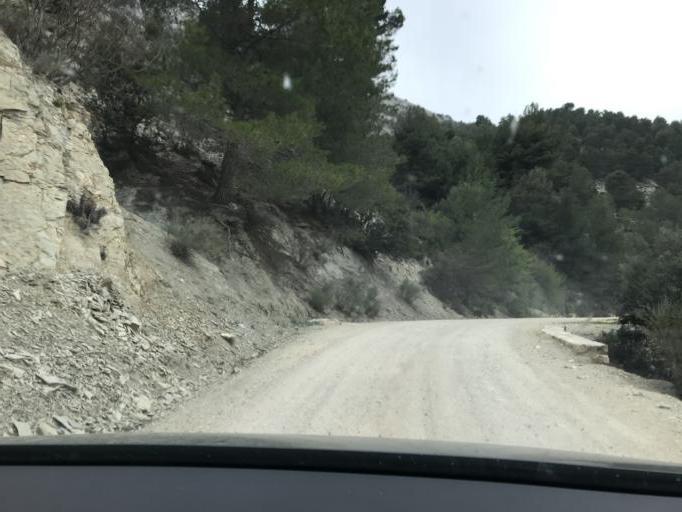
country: ES
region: Andalusia
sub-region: Provincia de Granada
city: Castril
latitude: 37.8520
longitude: -2.7753
